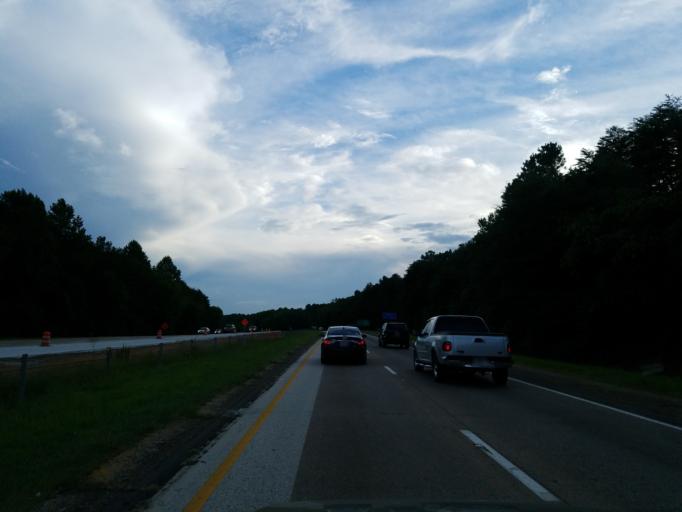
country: US
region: Georgia
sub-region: Forsyth County
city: Cumming
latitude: 34.2144
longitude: -84.1186
